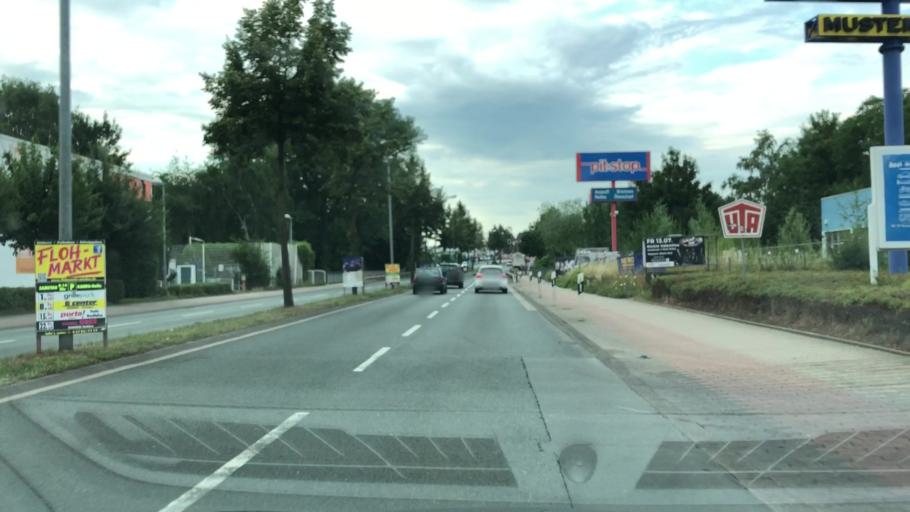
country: DE
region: North Rhine-Westphalia
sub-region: Regierungsbezirk Detmold
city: Minden
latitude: 52.2833
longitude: 8.9017
